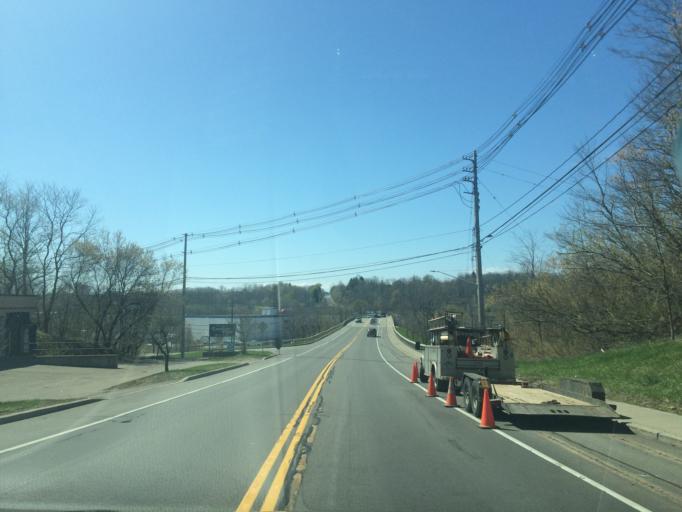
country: US
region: New York
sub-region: Monroe County
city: Fairport
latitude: 43.1014
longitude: -77.4322
